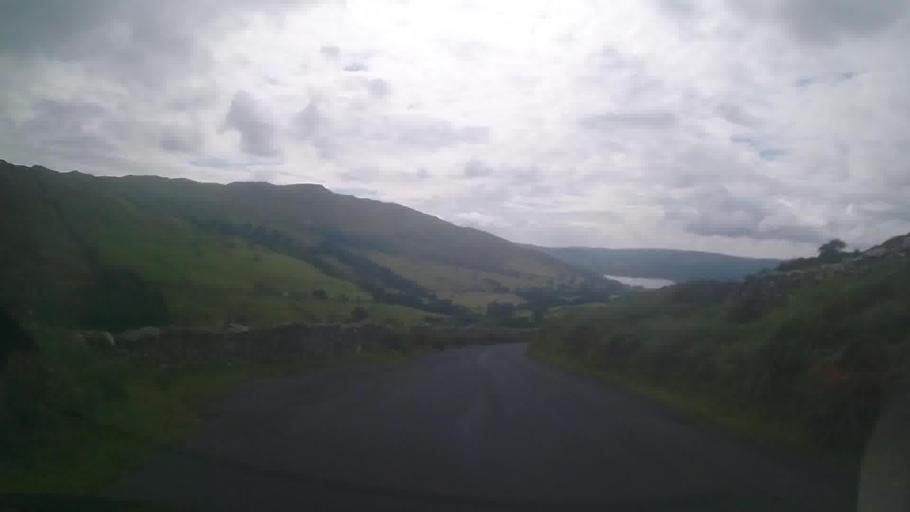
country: GB
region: England
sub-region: Cumbria
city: Ambleside
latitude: 54.4465
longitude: -2.9414
